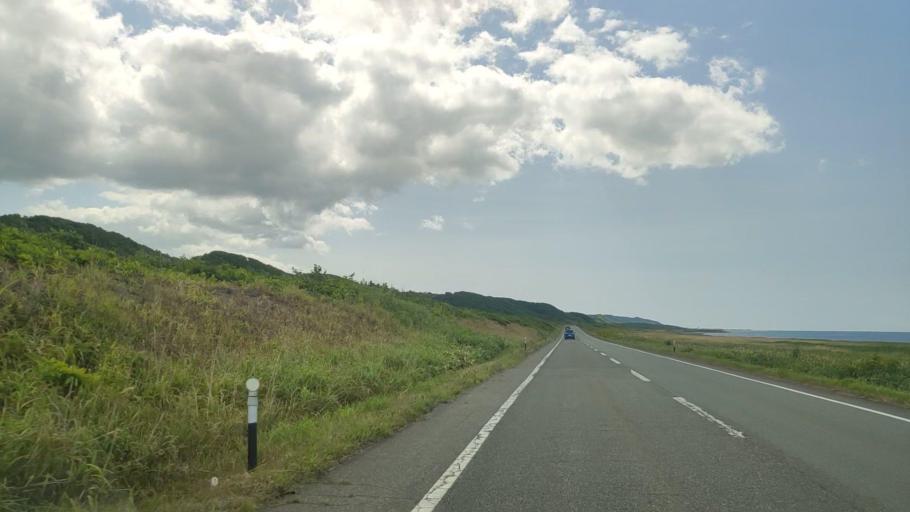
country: JP
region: Hokkaido
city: Wakkanai
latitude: 45.2780
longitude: 141.6153
